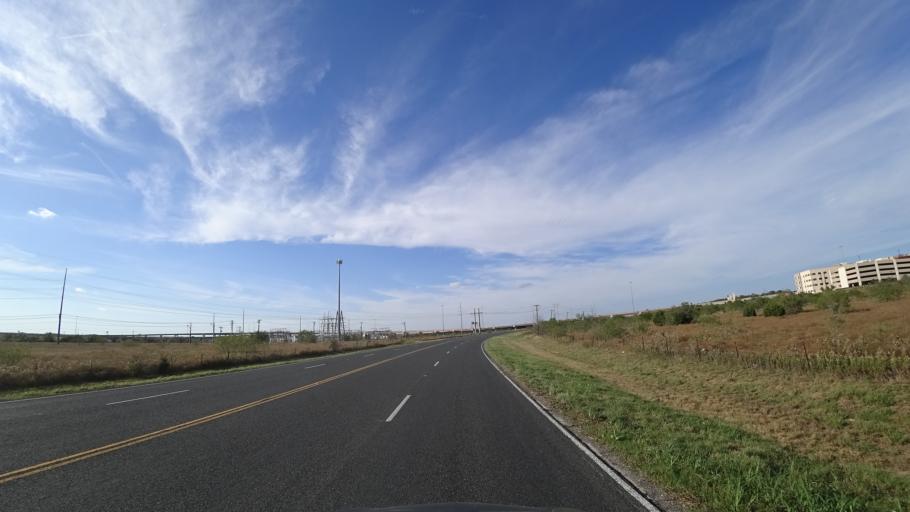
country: US
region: Texas
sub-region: Travis County
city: Wells Branch
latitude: 30.4732
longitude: -97.6916
